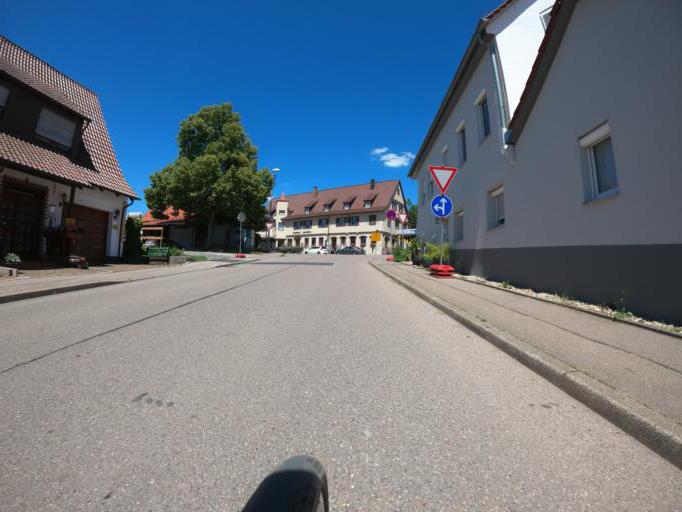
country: DE
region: Baden-Wuerttemberg
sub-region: Regierungsbezirk Stuttgart
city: Sersheim
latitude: 48.9987
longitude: 9.0218
